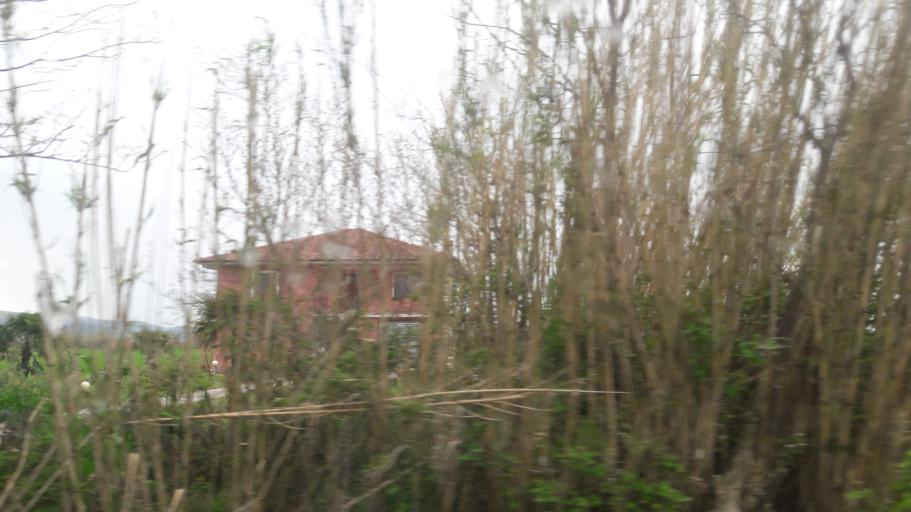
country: AL
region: Shkoder
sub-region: Rrethi i Shkodres
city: Berdica e Madhe
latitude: 41.9656
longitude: 19.4998
